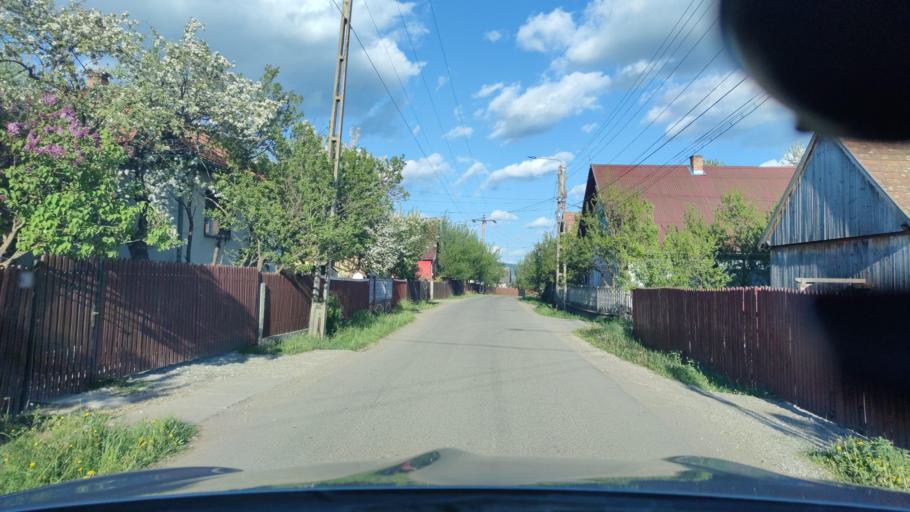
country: RO
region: Harghita
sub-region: Comuna Remetea
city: Remetea
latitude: 46.7968
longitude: 25.4403
